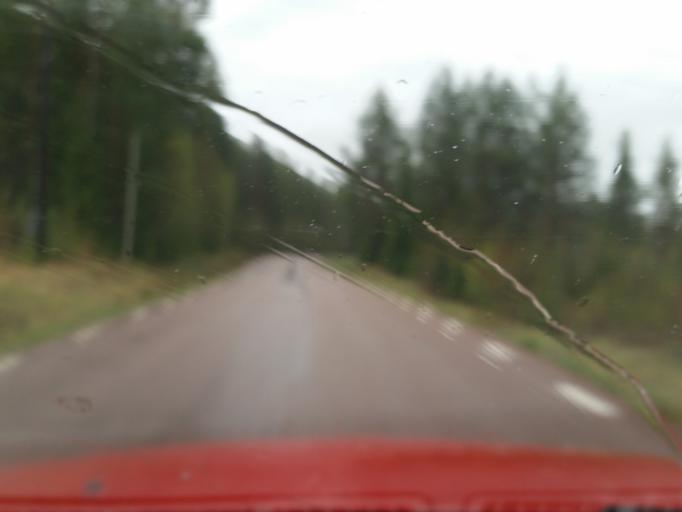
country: SE
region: Dalarna
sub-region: Gagnefs Kommun
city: Gagnef
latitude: 60.6757
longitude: 15.1717
